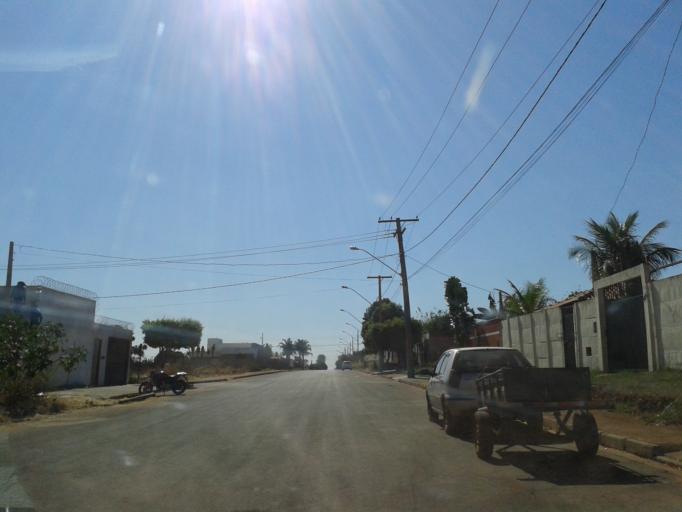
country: BR
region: Minas Gerais
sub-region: Ituiutaba
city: Ituiutaba
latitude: -18.9952
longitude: -49.4591
